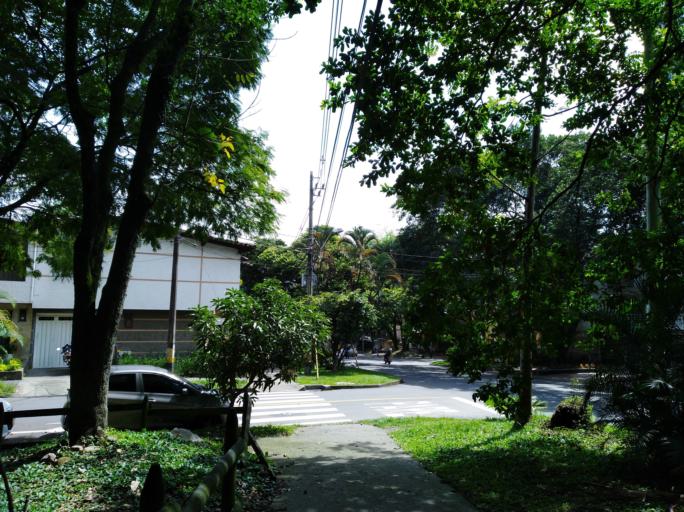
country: CO
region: Antioquia
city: Medellin
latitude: 6.2442
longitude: -75.6125
